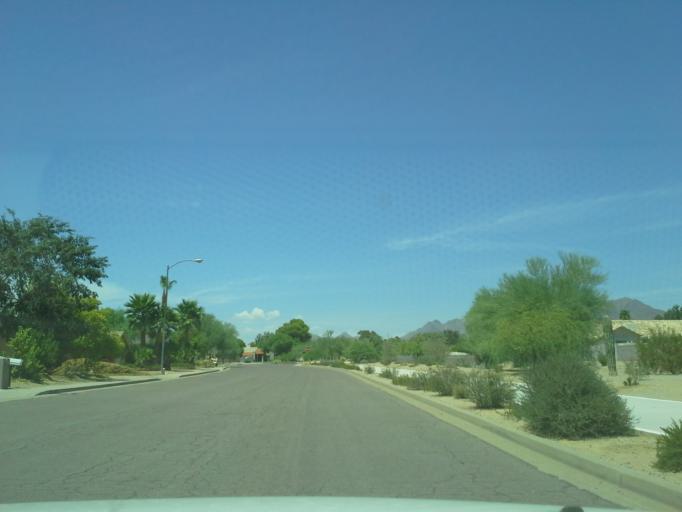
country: US
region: Arizona
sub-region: Maricopa County
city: Scottsdale
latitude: 33.5921
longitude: -111.8771
